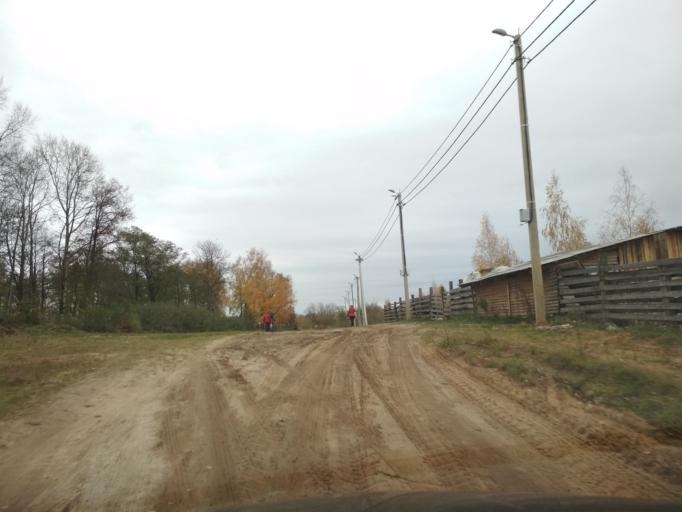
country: BY
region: Minsk
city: Blon'
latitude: 53.5204
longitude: 28.1775
